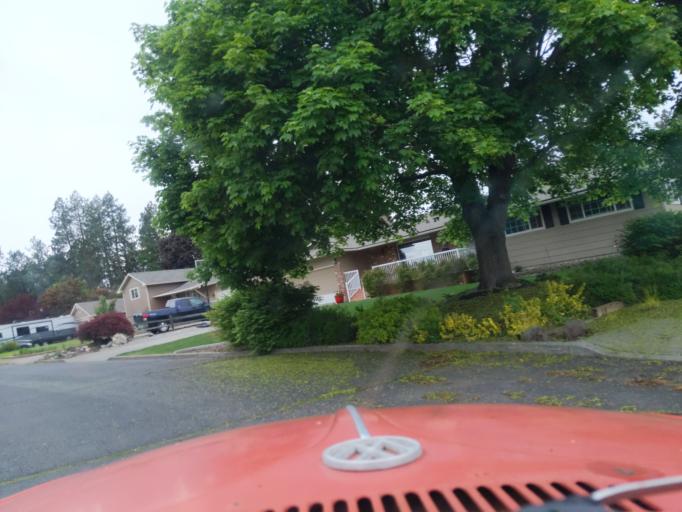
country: US
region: Washington
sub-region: Spokane County
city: Spokane
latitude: 47.6182
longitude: -117.3704
